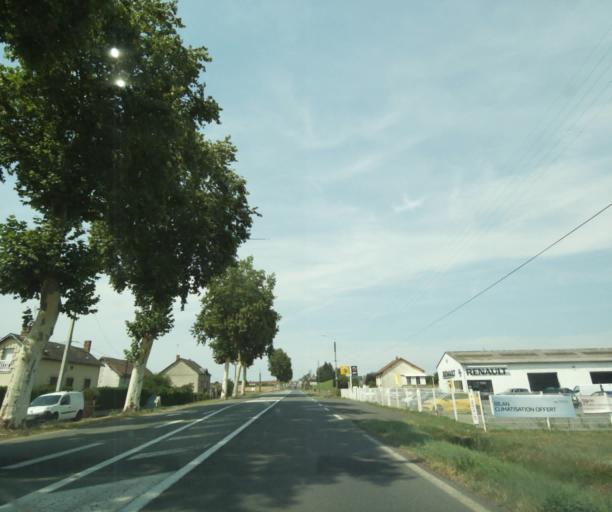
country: FR
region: Centre
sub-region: Departement d'Indre-et-Loire
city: La Celle-Saint-Avant
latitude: 47.0144
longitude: 0.6023
